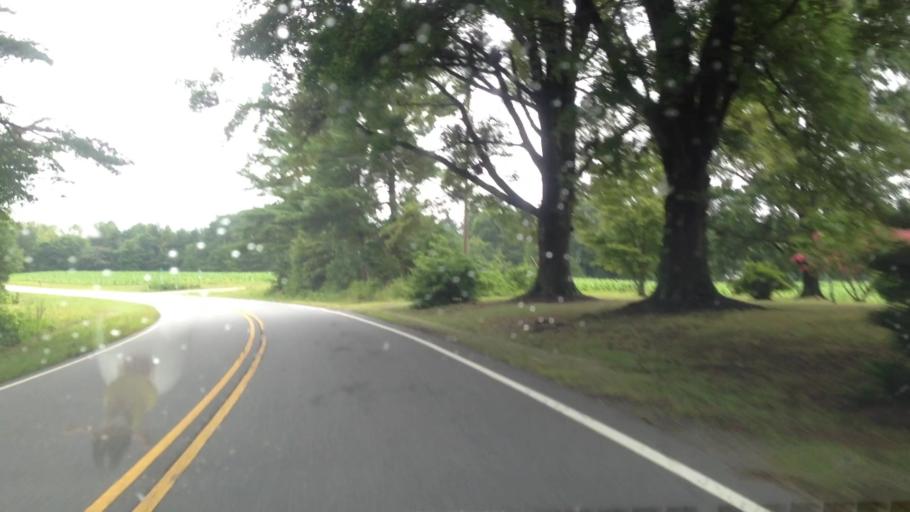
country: US
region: North Carolina
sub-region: Rockingham County
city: Mayodan
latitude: 36.4040
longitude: -80.0424
